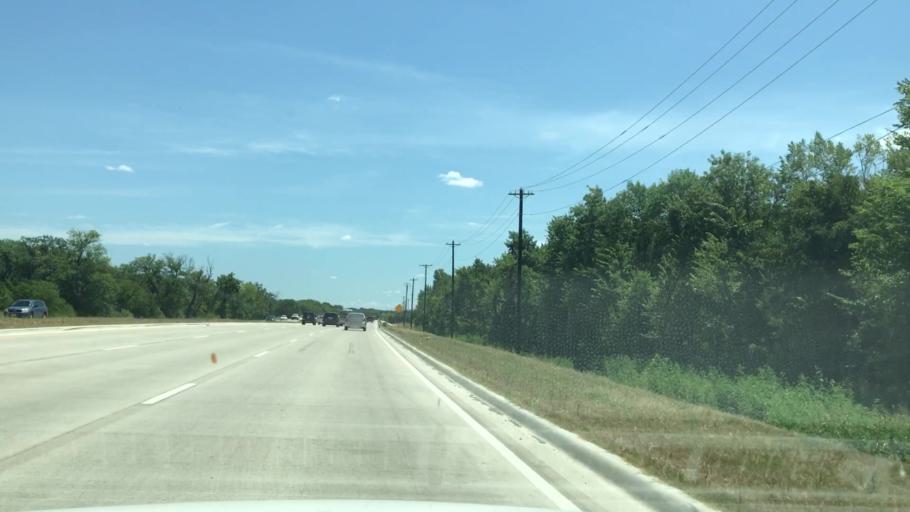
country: US
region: Texas
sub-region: Collin County
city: Lavon
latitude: 33.0246
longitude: -96.4801
